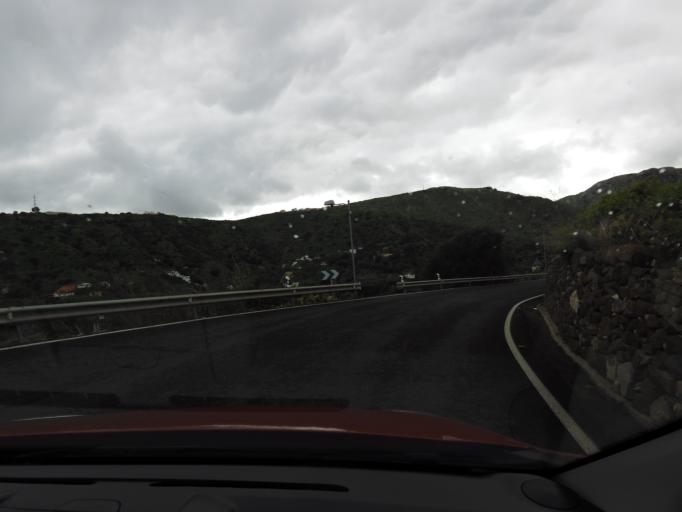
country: ES
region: Canary Islands
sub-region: Provincia de Las Palmas
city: Santa Brigida
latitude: 28.0245
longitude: -15.4711
